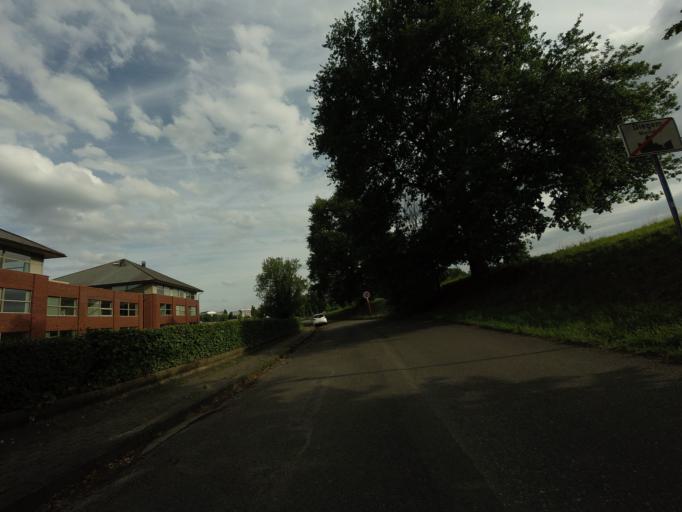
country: BE
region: Flanders
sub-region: Provincie Vlaams-Brabant
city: Diegem
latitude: 50.8882
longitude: 4.4437
